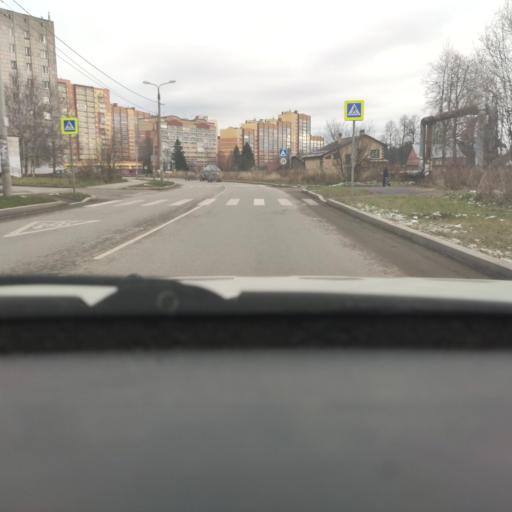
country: RU
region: Perm
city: Perm
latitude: 58.0853
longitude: 56.3992
